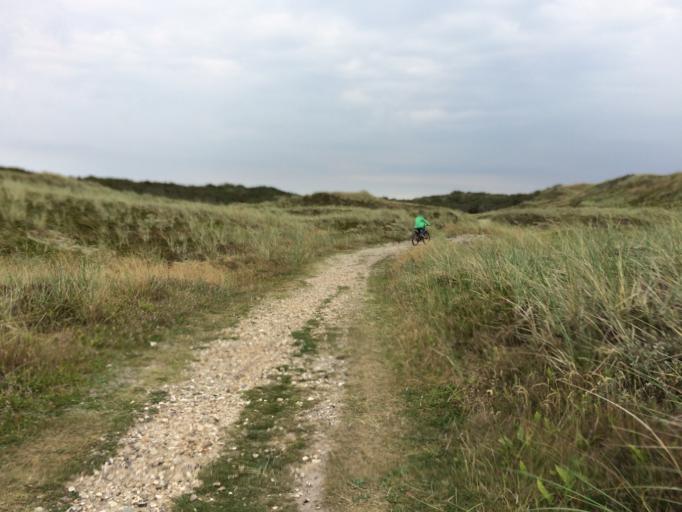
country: DK
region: Central Jutland
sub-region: Holstebro Kommune
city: Ulfborg
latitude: 56.2879
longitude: 8.1297
